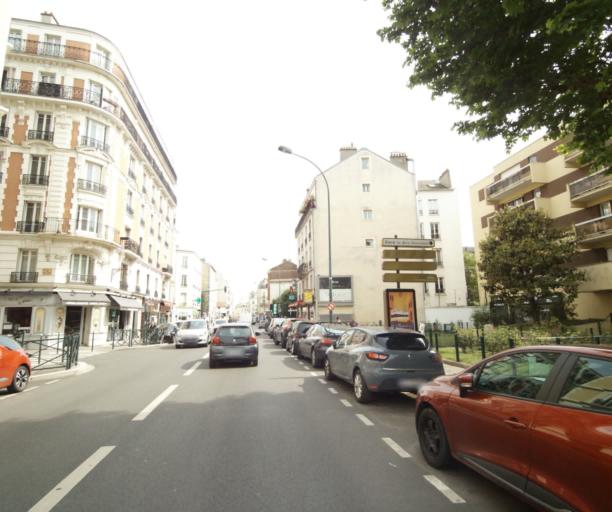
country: FR
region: Ile-de-France
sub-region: Departement des Hauts-de-Seine
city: Asnieres-sur-Seine
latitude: 48.9107
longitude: 2.2857
